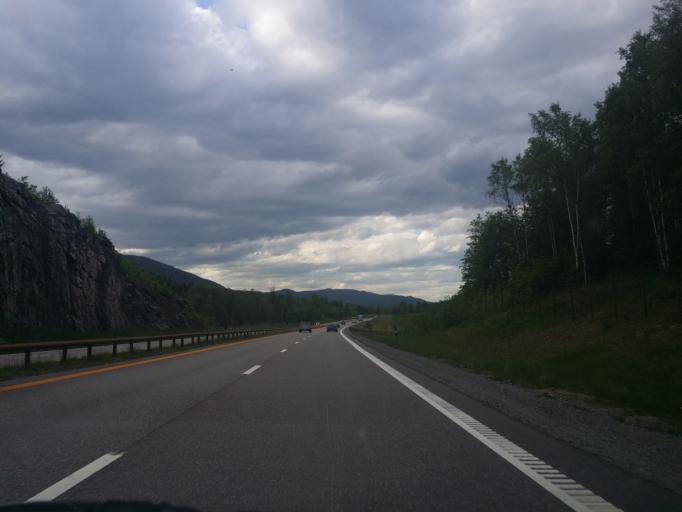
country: NO
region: Akershus
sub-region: Eidsvoll
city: Eidsvoll
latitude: 60.3563
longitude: 11.2065
